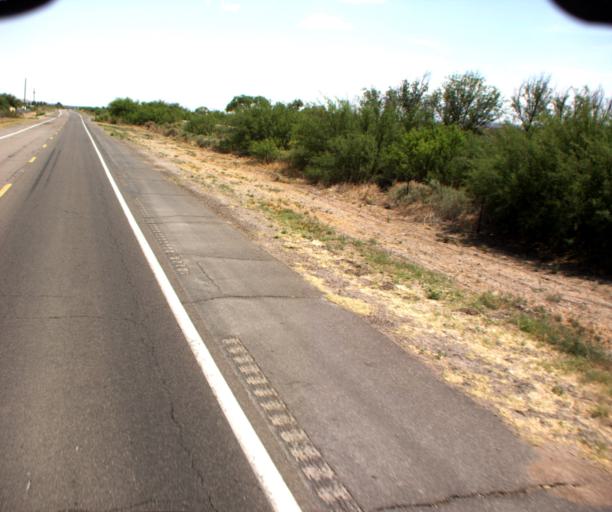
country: US
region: Arizona
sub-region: Greenlee County
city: Clifton
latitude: 32.6862
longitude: -109.0835
